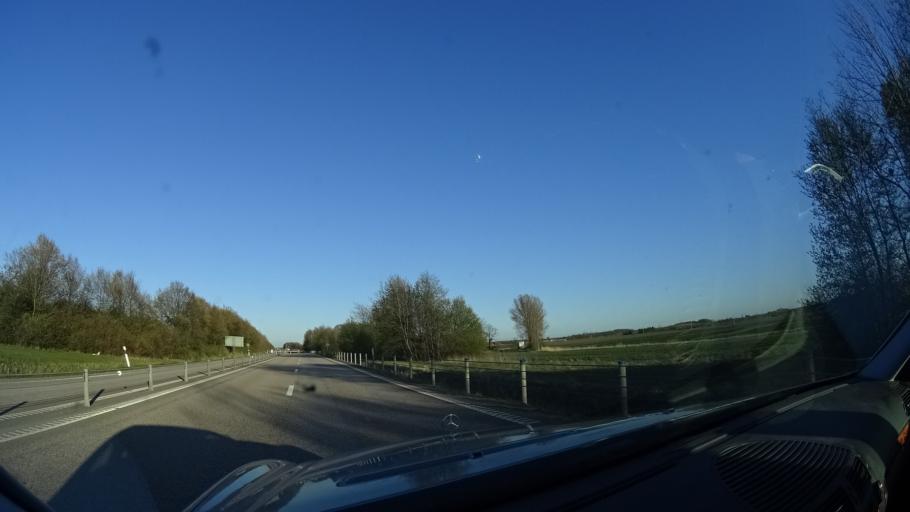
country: SE
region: Skane
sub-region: Bjuvs Kommun
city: Bjuv
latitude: 56.0796
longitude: 12.8933
